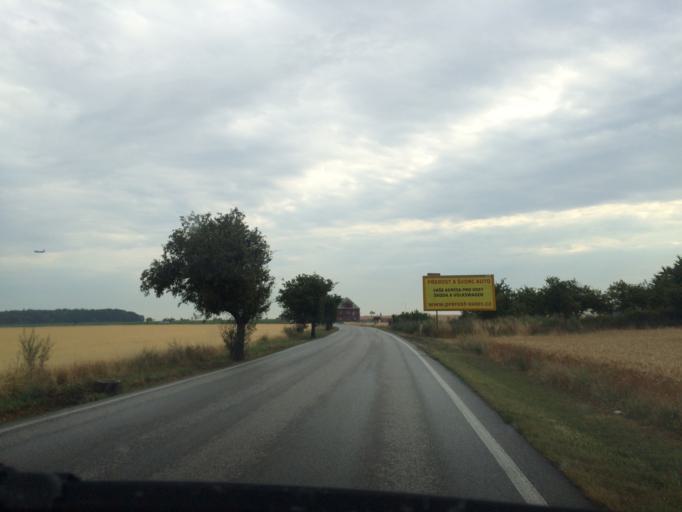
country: CZ
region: Central Bohemia
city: Tuchomerice
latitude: 50.1124
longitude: 14.3082
